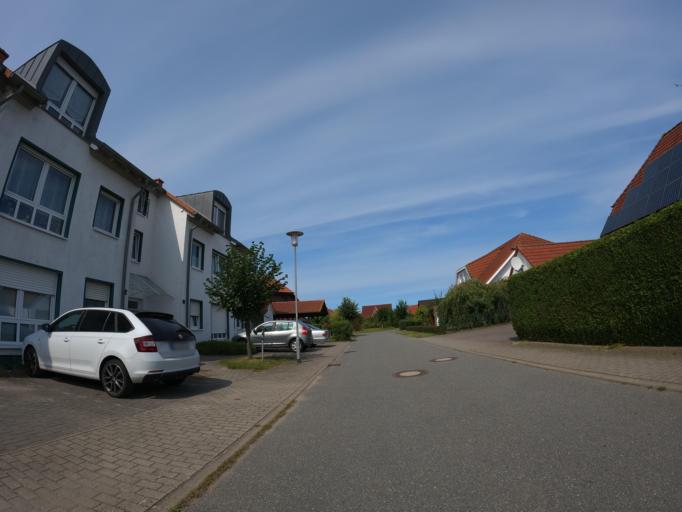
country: DE
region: Mecklenburg-Vorpommern
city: Altefahr
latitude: 54.3298
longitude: 13.1317
